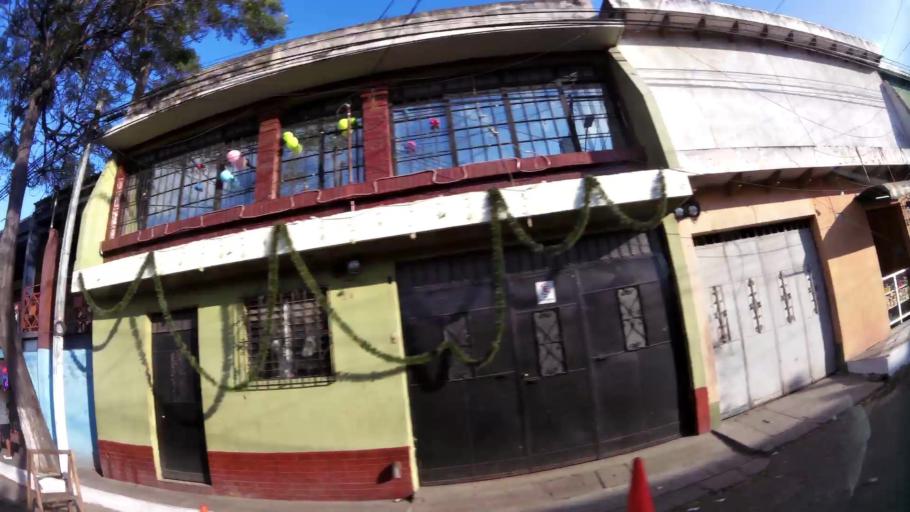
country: GT
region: Guatemala
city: Villa Nueva
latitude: 14.5192
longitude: -90.5796
